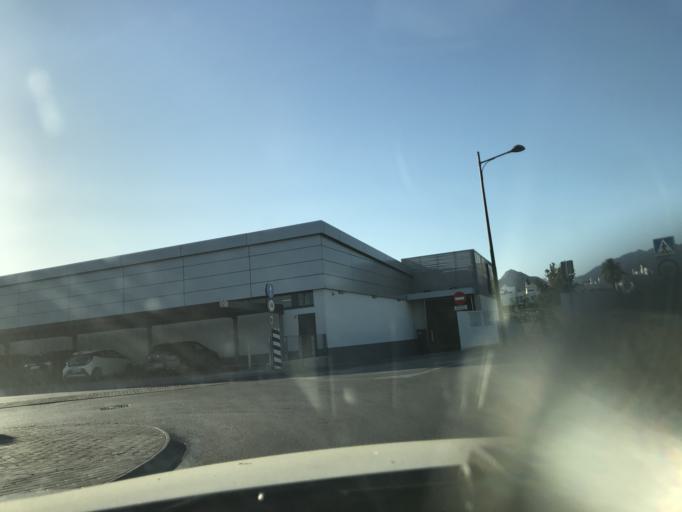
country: ES
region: Andalusia
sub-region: Provincia de Malaga
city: Benahavis
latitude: 36.4627
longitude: -5.0428
